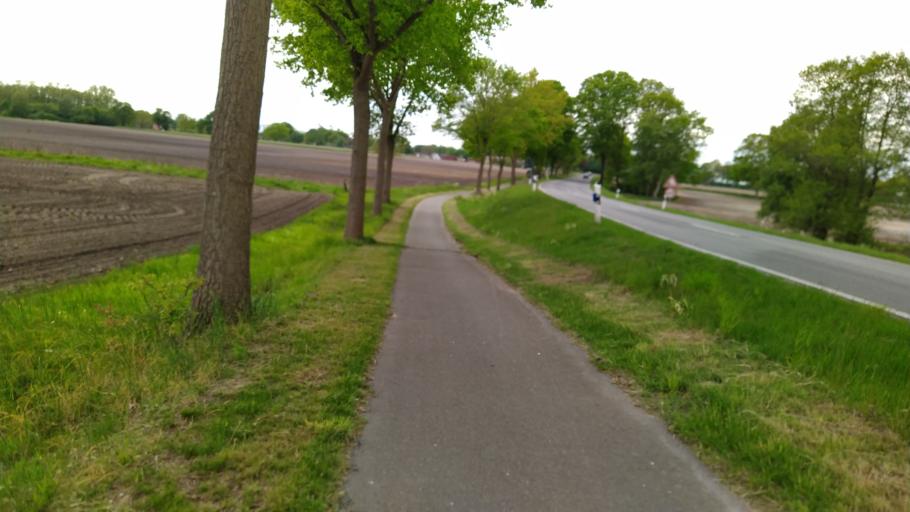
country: DE
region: Lower Saxony
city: Kirchtimke
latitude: 53.2558
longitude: 9.1672
